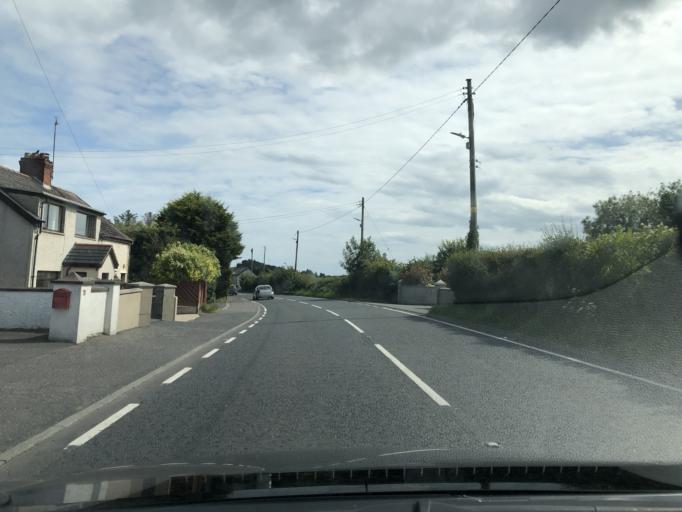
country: GB
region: Northern Ireland
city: Ballynahinch
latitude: 54.3763
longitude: -5.8677
